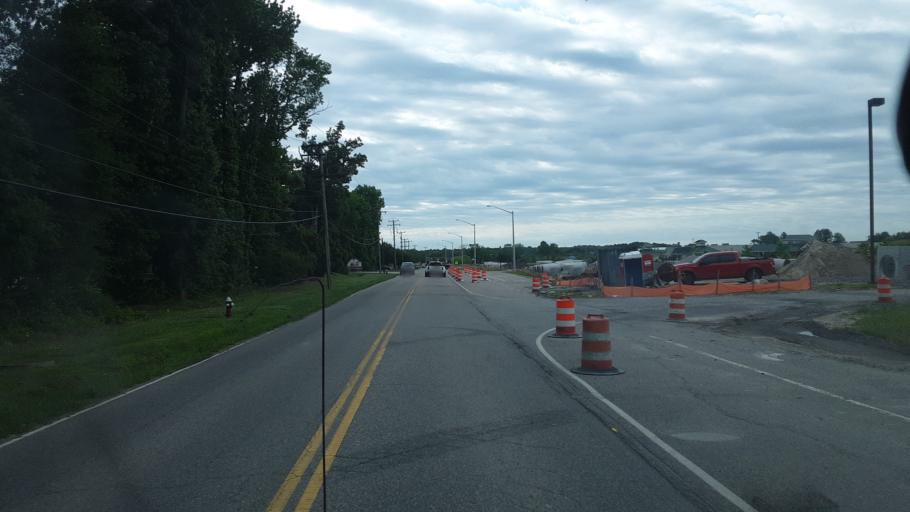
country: US
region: Virginia
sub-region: City of Virginia Beach
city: Virginia Beach
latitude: 36.7499
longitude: -76.0072
